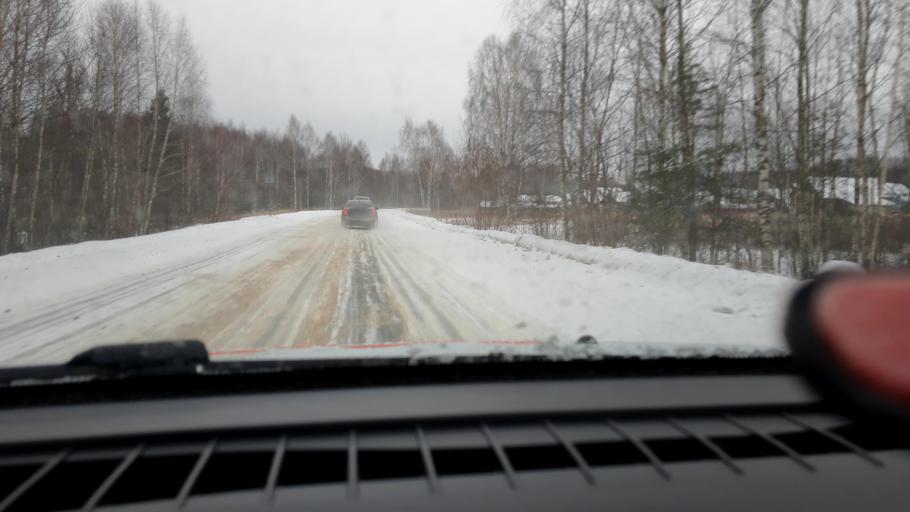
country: RU
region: Nizjnij Novgorod
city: Pamyat' Parizhskoy Kommuny
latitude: 56.2460
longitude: 44.4929
